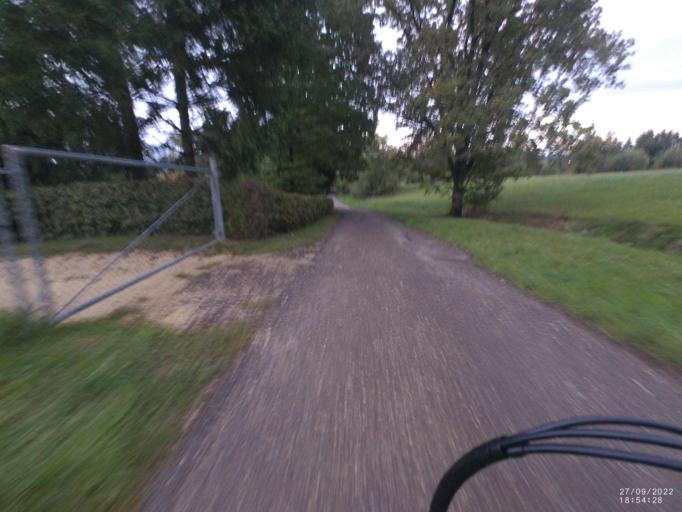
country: DE
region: Baden-Wuerttemberg
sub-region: Regierungsbezirk Stuttgart
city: Rechberghausen
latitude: 48.7264
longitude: 9.6311
